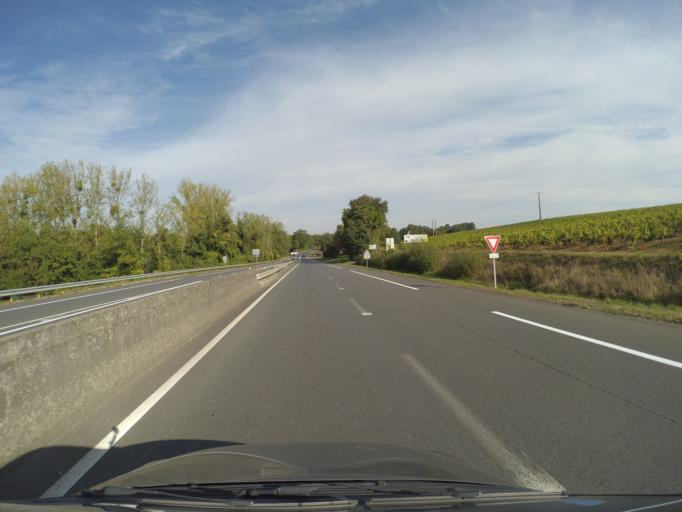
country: FR
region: Pays de la Loire
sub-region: Departement de la Loire-Atlantique
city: Clisson
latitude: 47.1035
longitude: -1.2823
